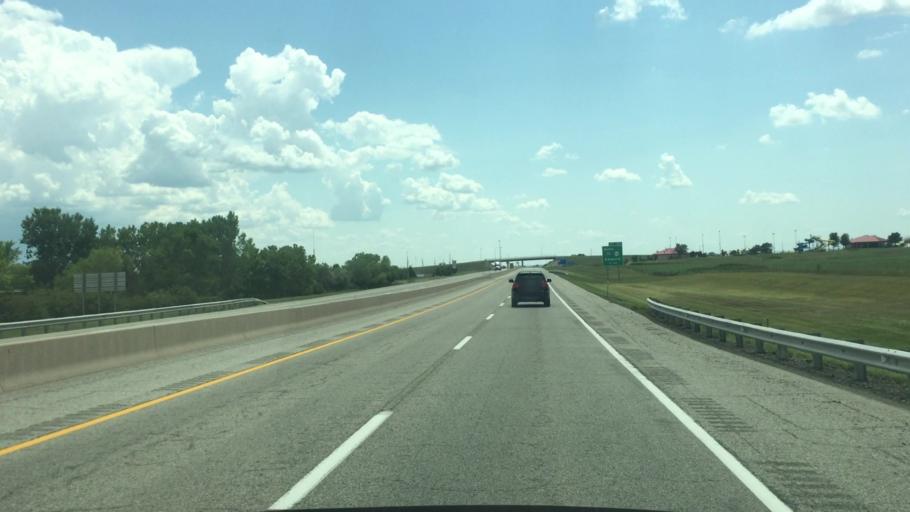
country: US
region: Kansas
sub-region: Lyon County
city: Emporia
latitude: 38.4252
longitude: -96.2287
